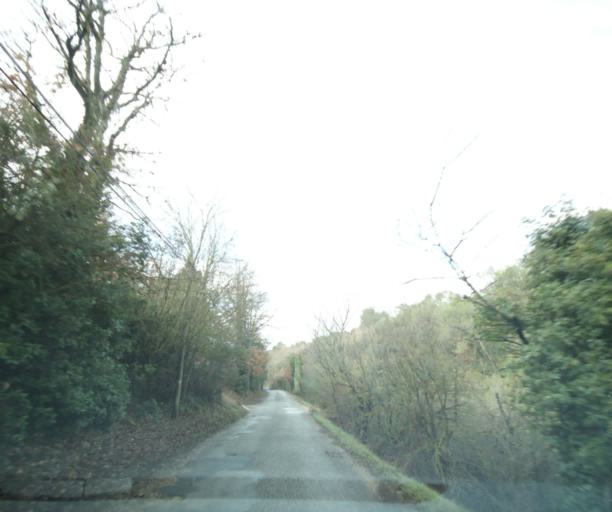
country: FR
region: Provence-Alpes-Cote d'Azur
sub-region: Departement du Var
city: Tourves
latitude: 43.4058
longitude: 5.9156
